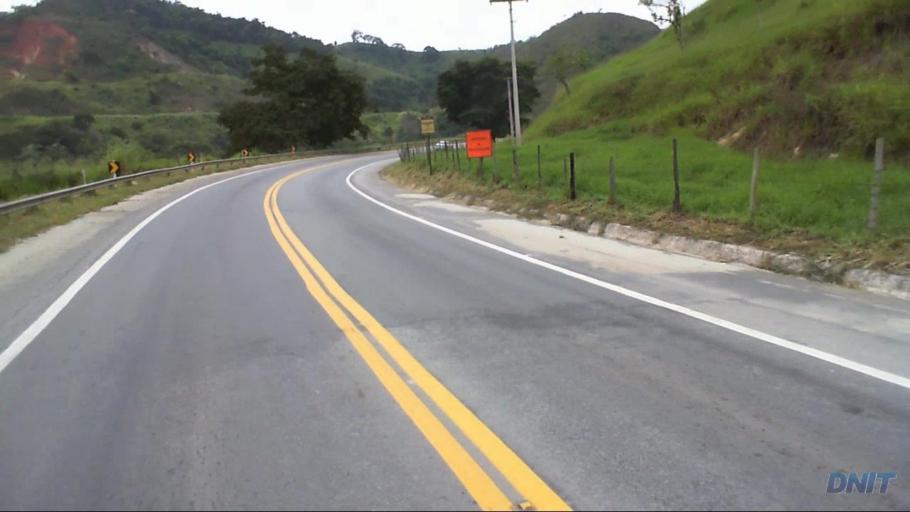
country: BR
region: Minas Gerais
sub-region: Timoteo
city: Timoteo
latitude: -19.6163
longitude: -42.7932
